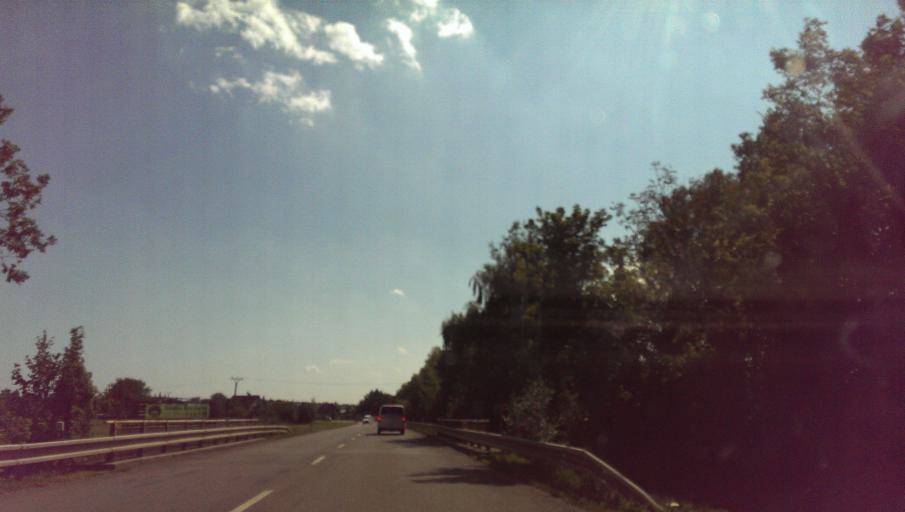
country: CZ
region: Zlin
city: Holesov
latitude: 49.3505
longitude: 17.6075
